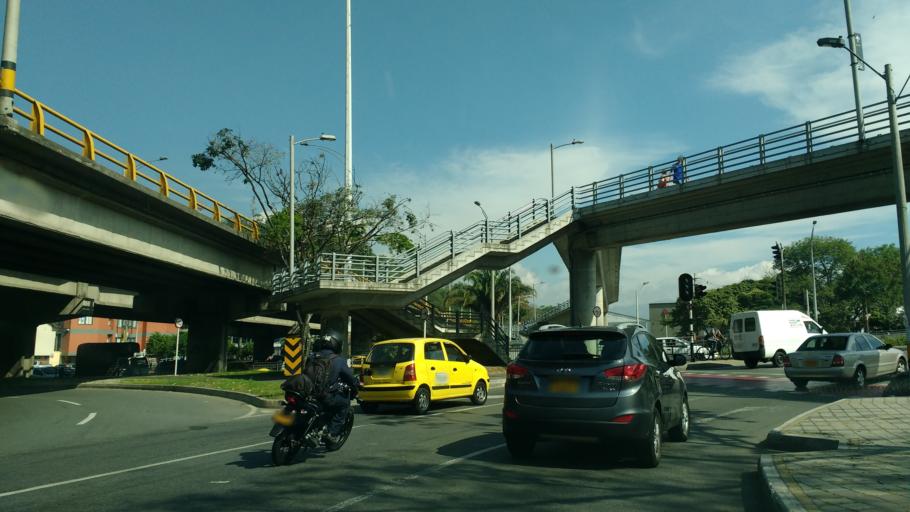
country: CO
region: Antioquia
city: Medellin
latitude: 6.2313
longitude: -75.5773
